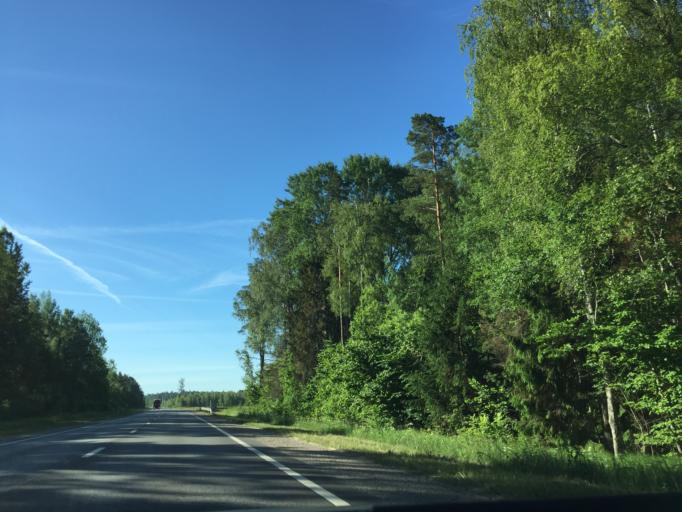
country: LV
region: Ventspils
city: Ventspils
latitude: 57.3886
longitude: 21.7037
